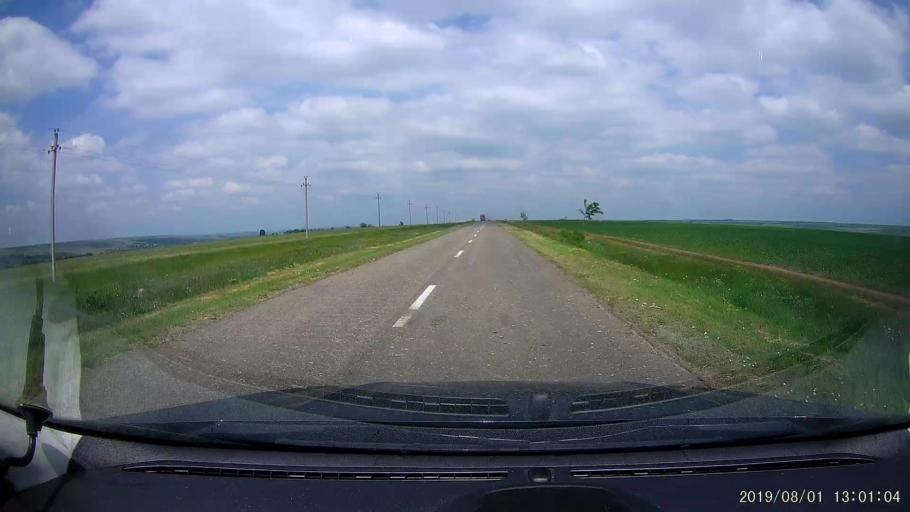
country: MD
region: Gagauzia
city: Vulcanesti
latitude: 45.7314
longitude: 28.3988
